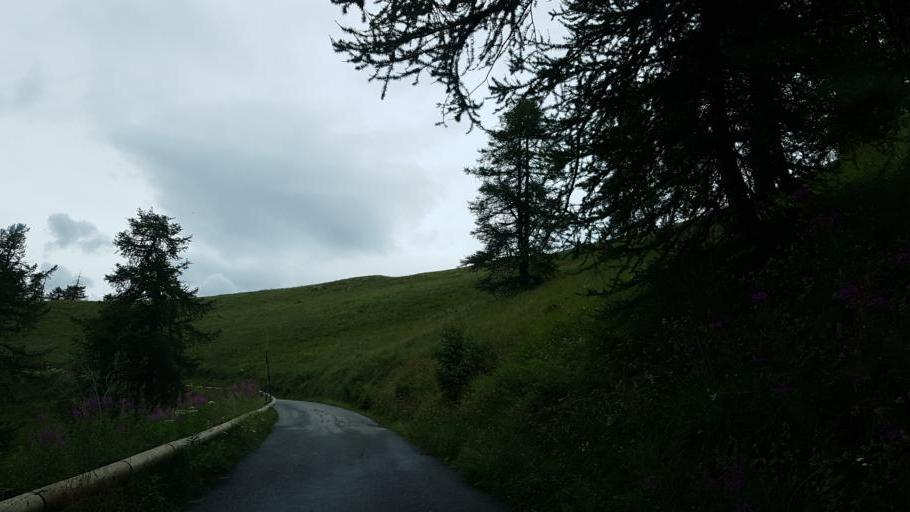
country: IT
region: Piedmont
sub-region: Provincia di Cuneo
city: Serre
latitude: 44.5244
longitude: 7.1039
